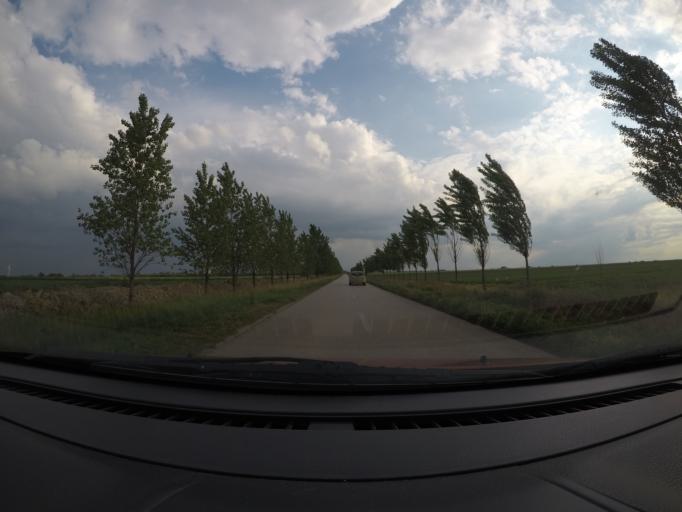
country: RS
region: Autonomna Pokrajina Vojvodina
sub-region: Juznobanatski Okrug
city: Kovacica
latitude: 45.0932
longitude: 20.6094
